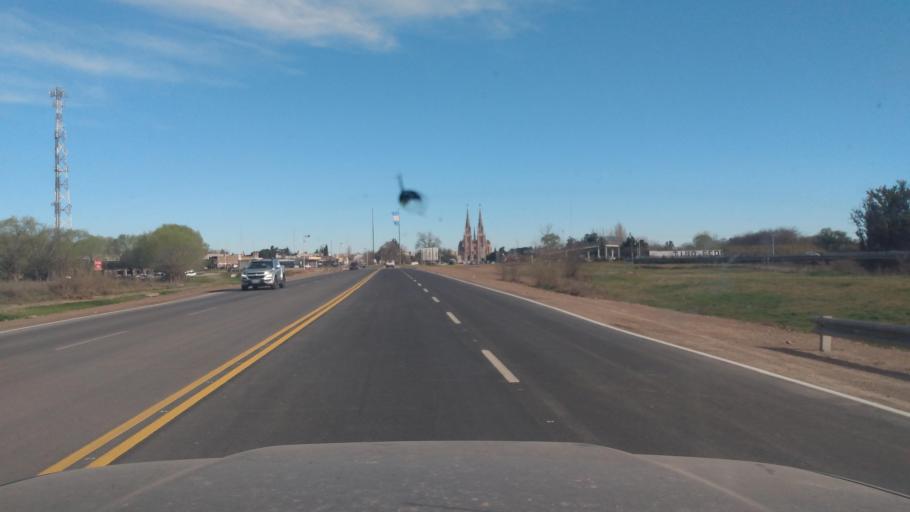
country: AR
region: Buenos Aires
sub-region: Partido de Lujan
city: Lujan
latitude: -34.5529
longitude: -59.1167
